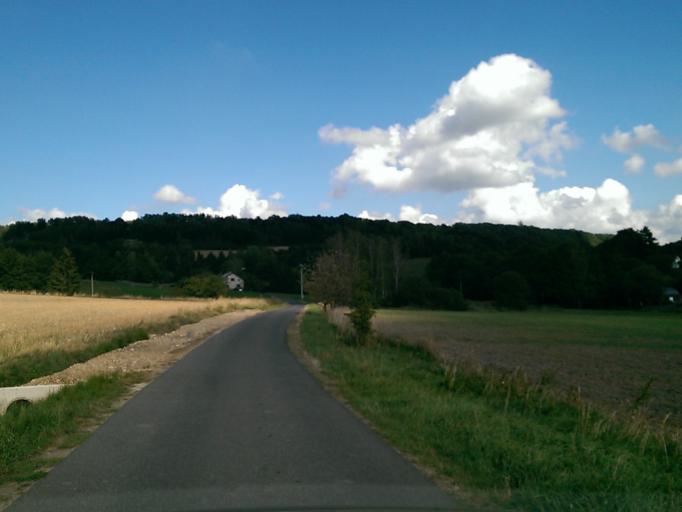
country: CZ
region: Central Bohemia
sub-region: Okres Mlada Boleslav
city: Zd'ar
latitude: 50.5444
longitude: 15.1247
